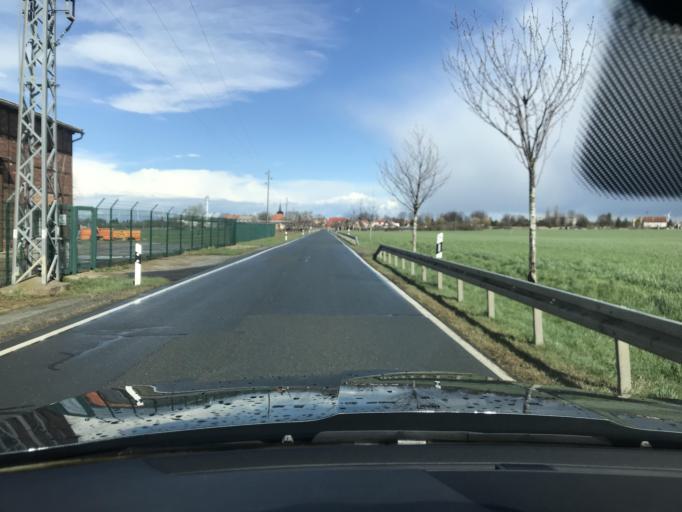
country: DE
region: Saxony-Anhalt
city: Hoym
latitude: 51.7269
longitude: 11.3337
